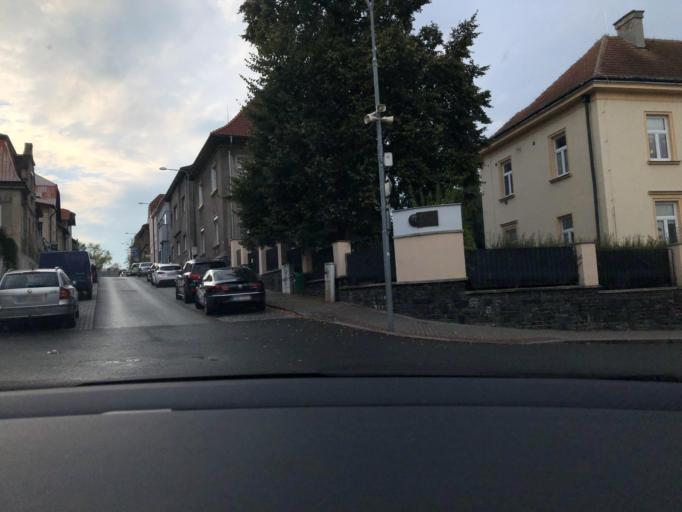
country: CZ
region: Central Bohemia
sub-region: Okres Kolin
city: Kolin
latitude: 50.0280
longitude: 15.1960
